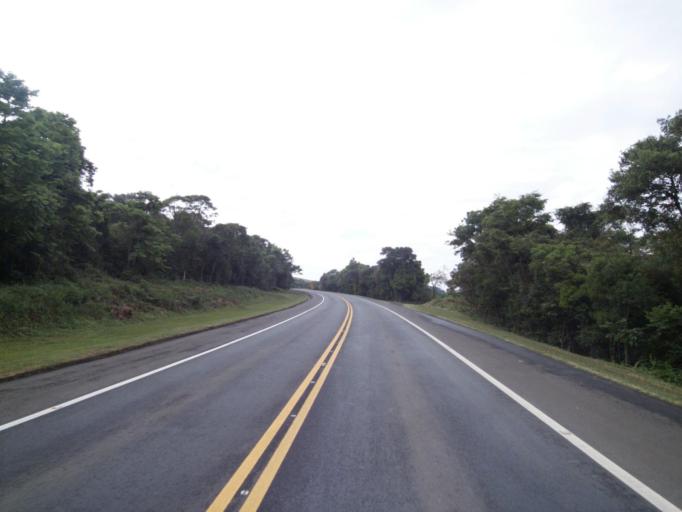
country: BR
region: Parana
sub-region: Irati
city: Irati
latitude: -25.4523
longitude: -50.6446
